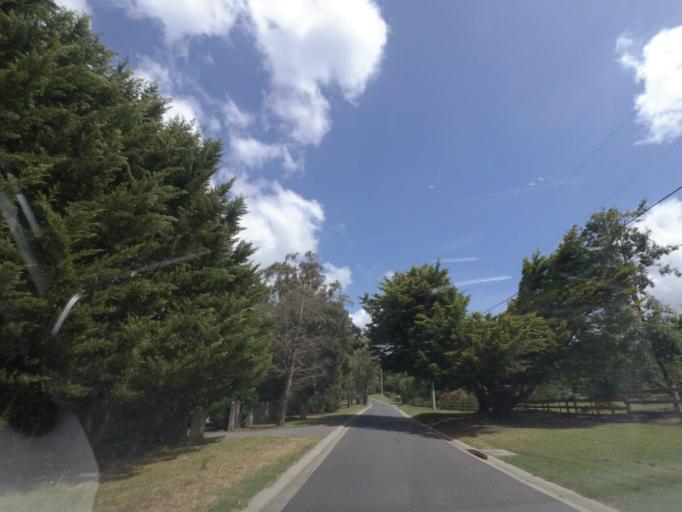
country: AU
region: Victoria
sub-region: Yarra Ranges
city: Mount Evelyn
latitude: -37.7801
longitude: 145.3589
